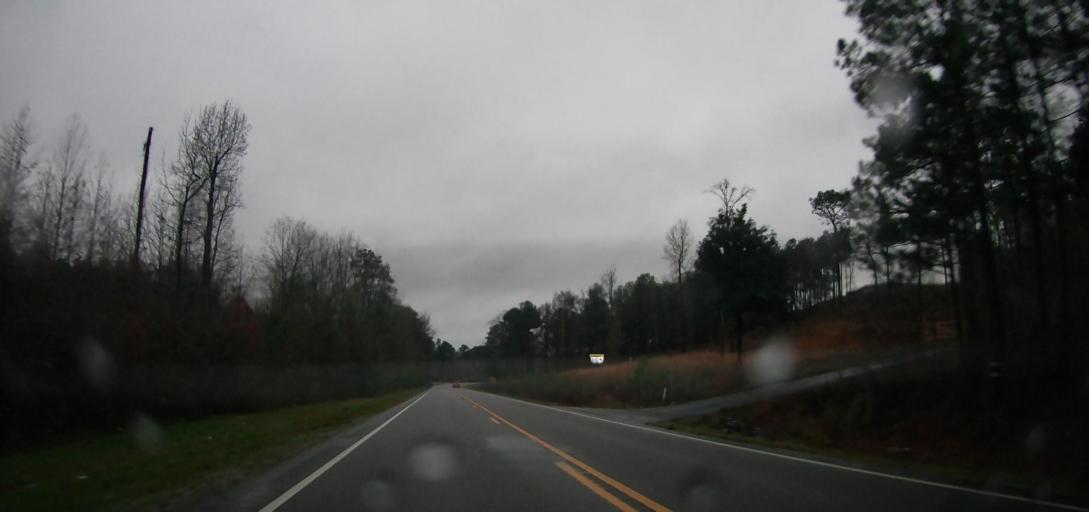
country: US
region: Alabama
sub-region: Bibb County
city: West Blocton
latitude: 33.0533
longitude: -87.1347
